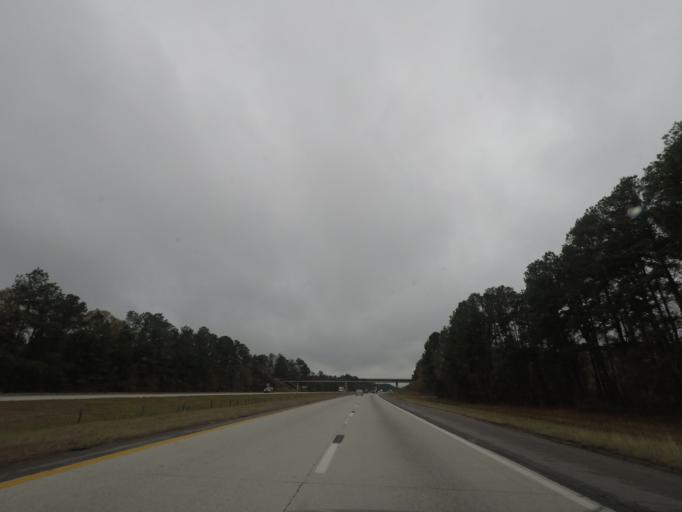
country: US
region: South Carolina
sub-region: Dorchester County
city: Saint George
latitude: 33.2972
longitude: -80.5572
